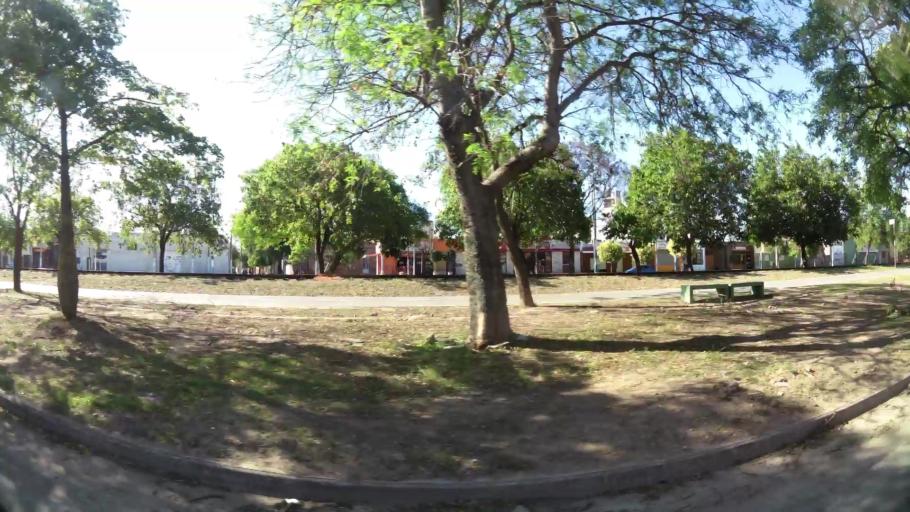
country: AR
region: Cordoba
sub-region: Departamento de Capital
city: Cordoba
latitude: -31.3938
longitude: -64.1526
